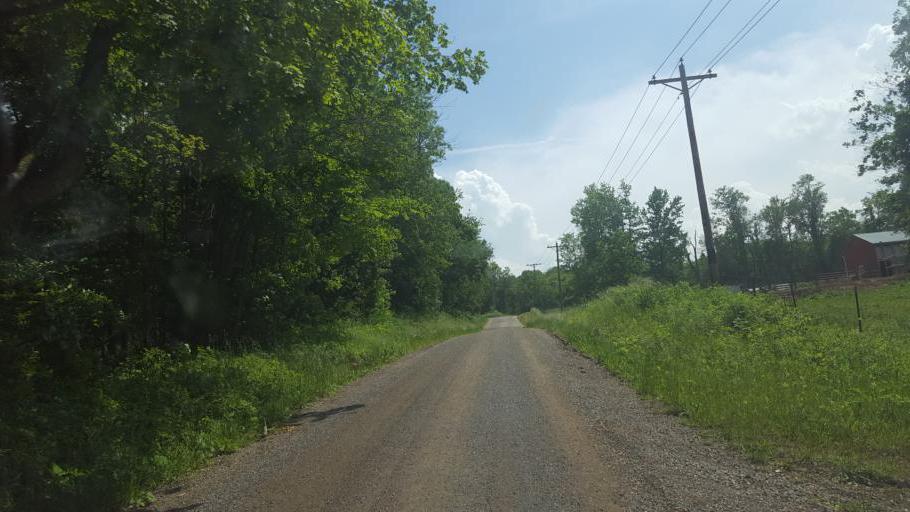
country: US
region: Ohio
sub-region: Knox County
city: Oak Hill
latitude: 40.3347
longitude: -82.2459
